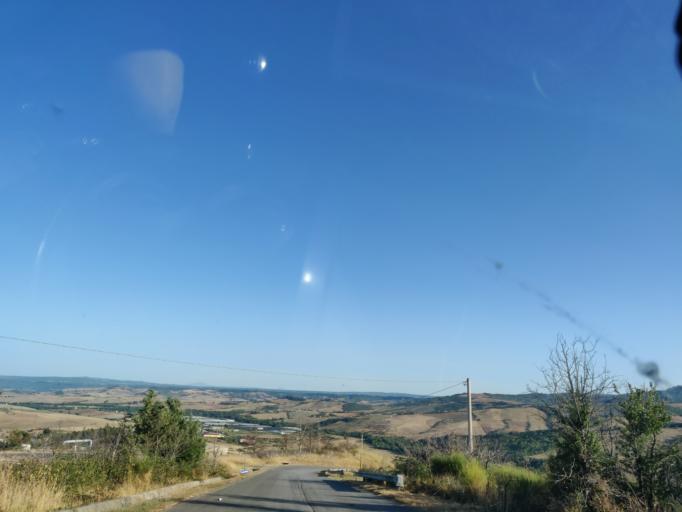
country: IT
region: Tuscany
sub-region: Provincia di Siena
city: Piancastagnaio
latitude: 42.8374
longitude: 11.7084
